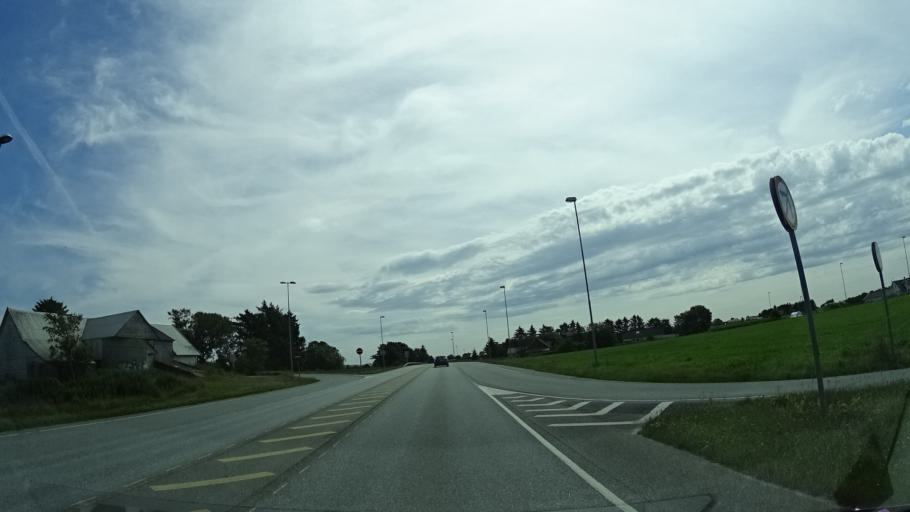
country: NO
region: Rogaland
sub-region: Randaberg
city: Randaberg
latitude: 59.0084
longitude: 5.6395
